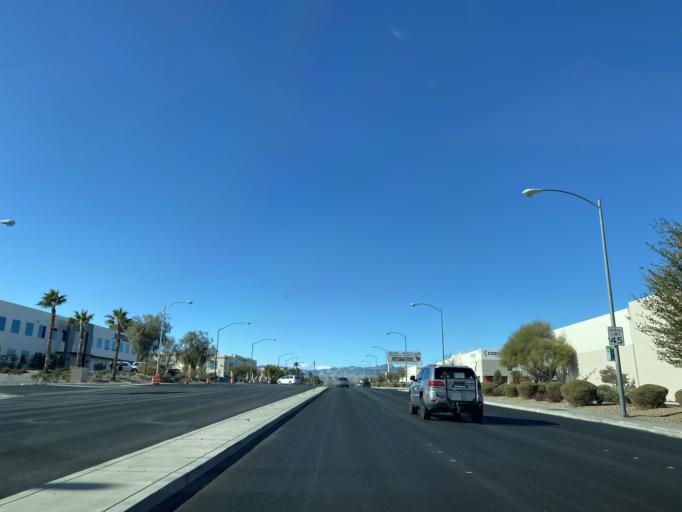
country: US
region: Nevada
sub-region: Clark County
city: Paradise
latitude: 36.0718
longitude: -115.1905
